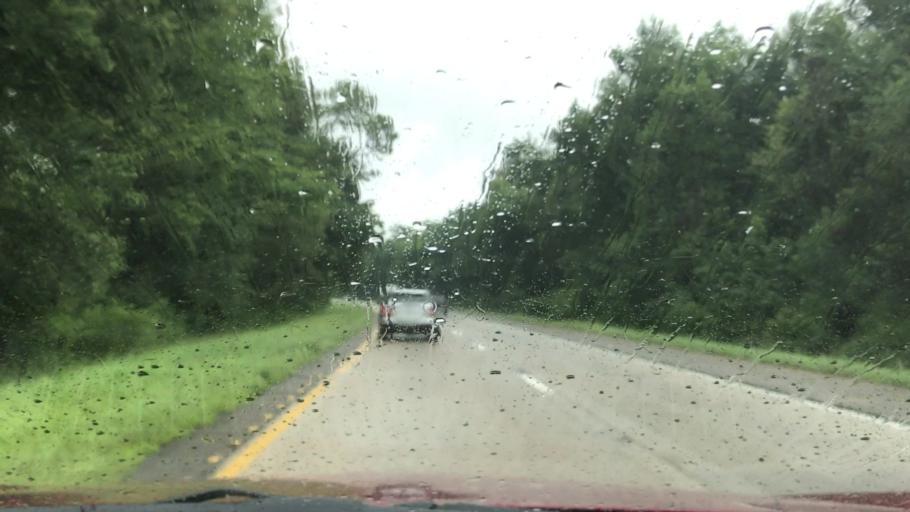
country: US
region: South Carolina
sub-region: Orangeburg County
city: Holly Hill
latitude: 33.2379
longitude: -80.4582
